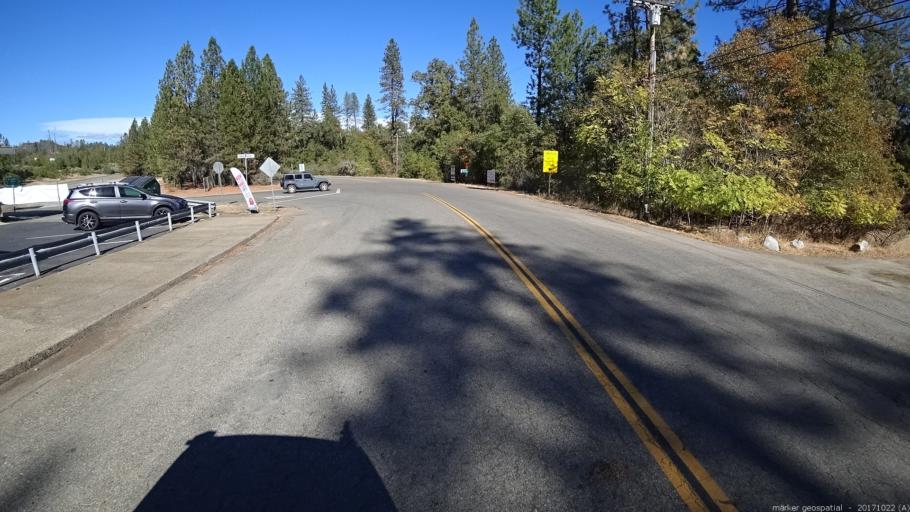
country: US
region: California
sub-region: Shasta County
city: Central Valley (historical)
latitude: 40.8922
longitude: -122.3819
